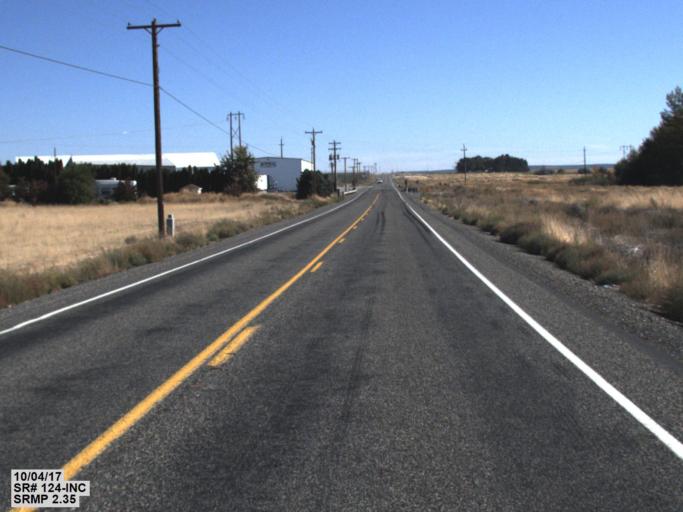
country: US
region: Washington
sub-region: Walla Walla County
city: Burbank
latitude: 46.2118
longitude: -118.9656
